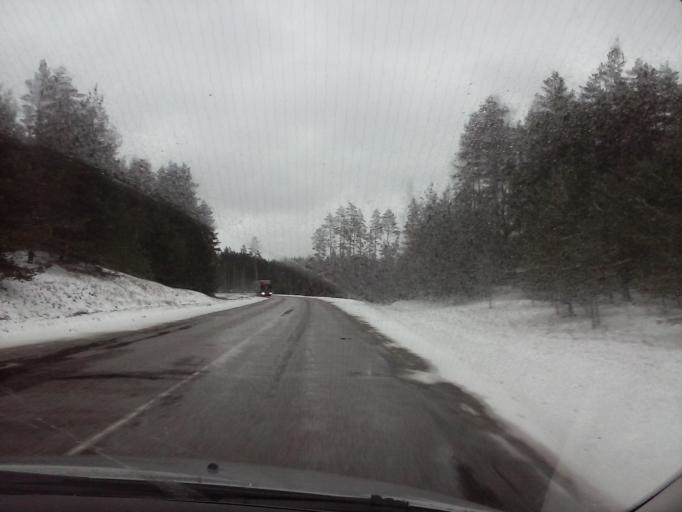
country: LV
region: Strenci
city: Seda
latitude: 57.6514
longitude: 25.8639
